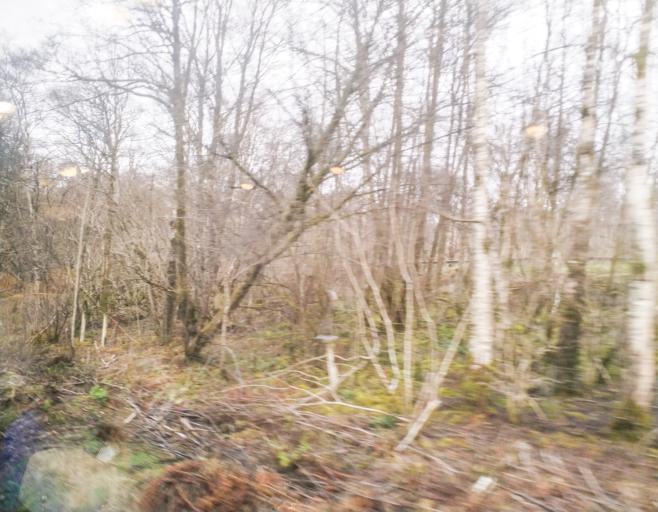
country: GB
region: Scotland
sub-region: Highland
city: Spean Bridge
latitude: 56.8920
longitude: -4.8810
